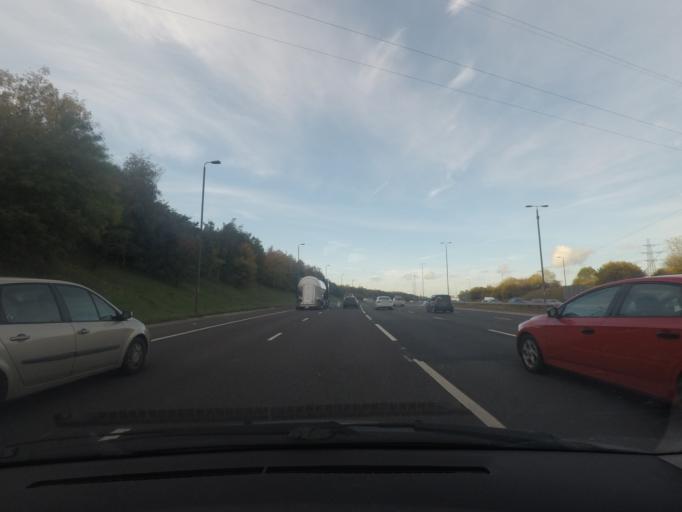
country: GB
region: England
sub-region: City and Borough of Leeds
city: Lofthouse
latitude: 53.7455
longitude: -1.5168
